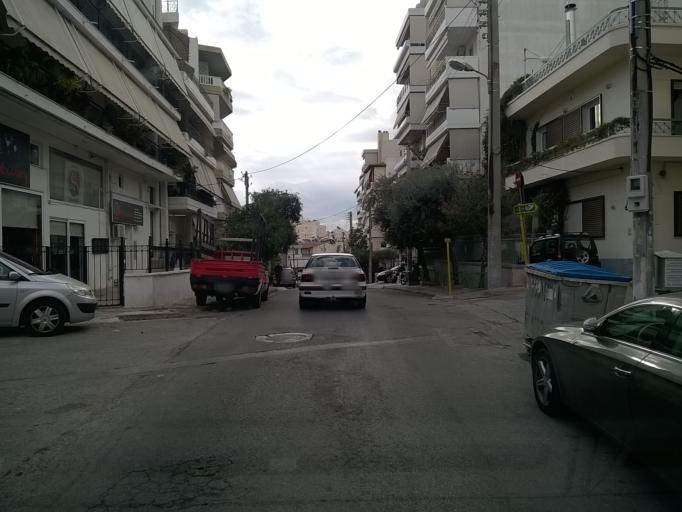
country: GR
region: Attica
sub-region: Nomarchia Athinas
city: Dhafni
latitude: 37.9452
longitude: 23.7283
